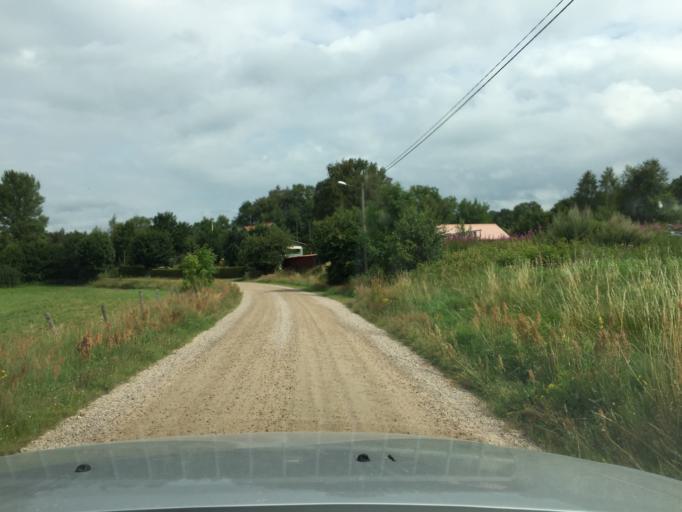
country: SE
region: Skane
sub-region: Hassleholms Kommun
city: Sosdala
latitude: 56.0264
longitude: 13.6838
